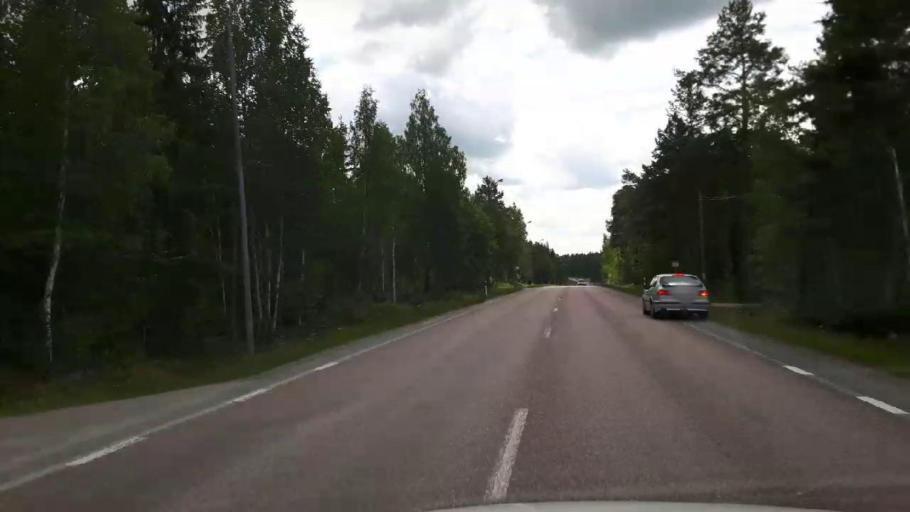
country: SE
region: Dalarna
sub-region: Faluns Kommun
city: Falun
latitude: 60.5146
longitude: 15.7358
